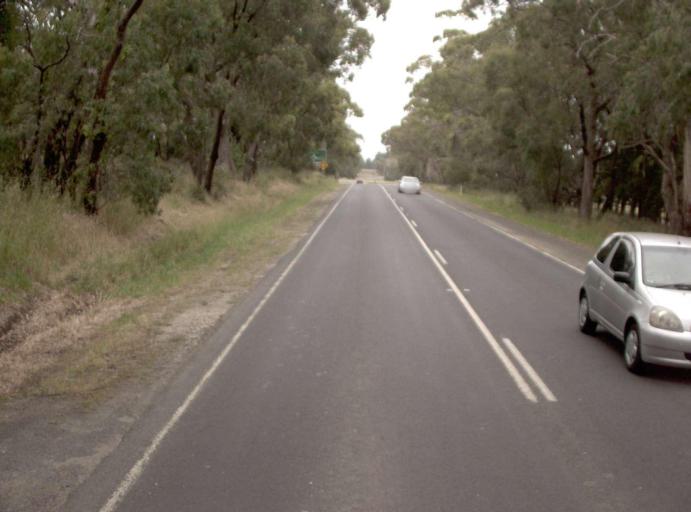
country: AU
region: Victoria
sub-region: Latrobe
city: Traralgon
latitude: -38.2531
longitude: 146.4923
